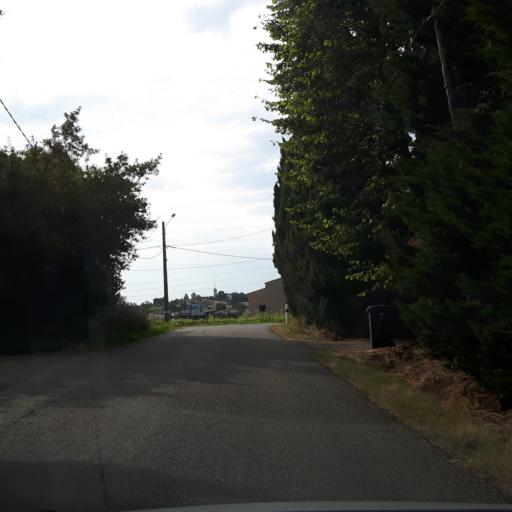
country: FR
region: Midi-Pyrenees
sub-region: Departement de la Haute-Garonne
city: Castelnau-d'Estretefonds
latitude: 43.7965
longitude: 1.3579
